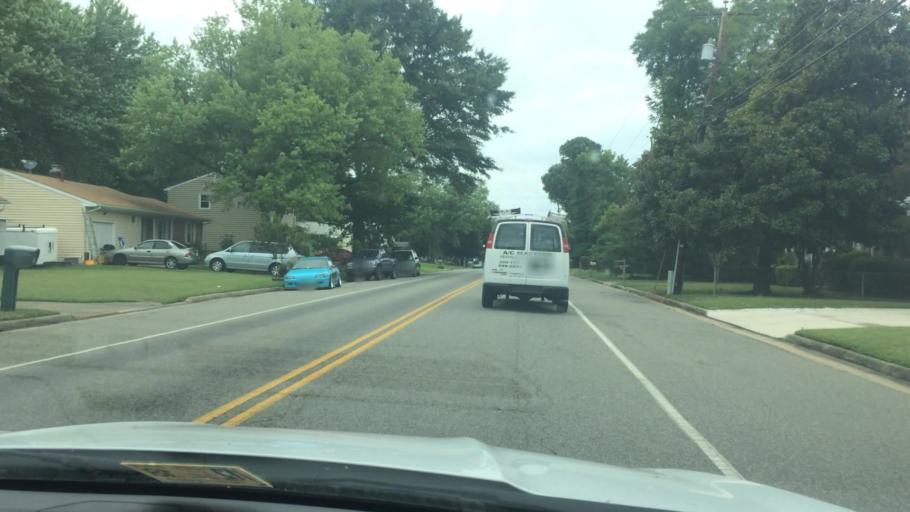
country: US
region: Virginia
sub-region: City of Williamsburg
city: Williamsburg
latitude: 37.2720
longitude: -76.6721
